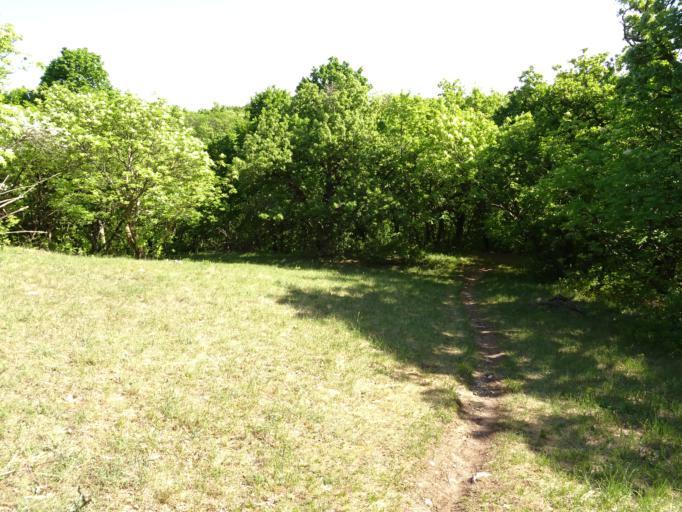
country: HU
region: Fejer
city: Csakvar
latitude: 47.3976
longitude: 18.4388
